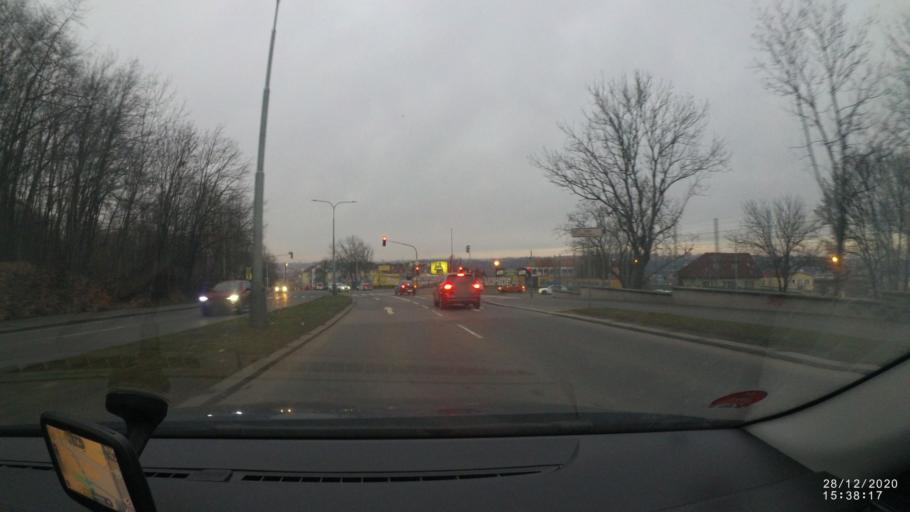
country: CZ
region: Praha
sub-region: Praha 9
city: Prosek
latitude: 50.0986
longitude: 14.4942
